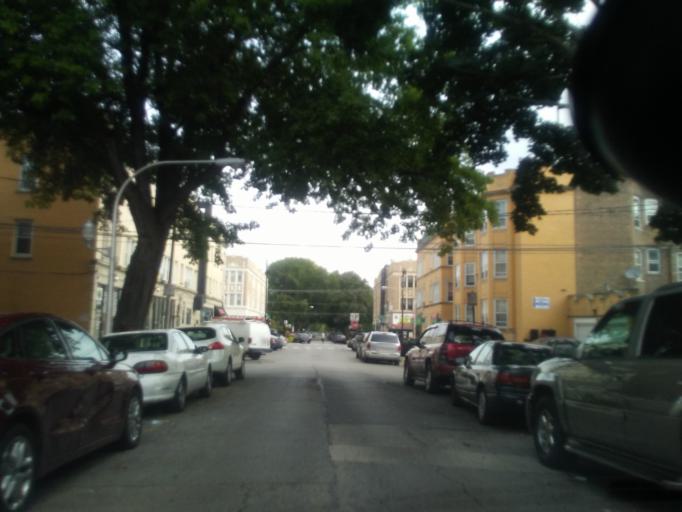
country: US
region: Illinois
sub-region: Cook County
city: Lincolnwood
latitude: 41.9971
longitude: -87.6875
